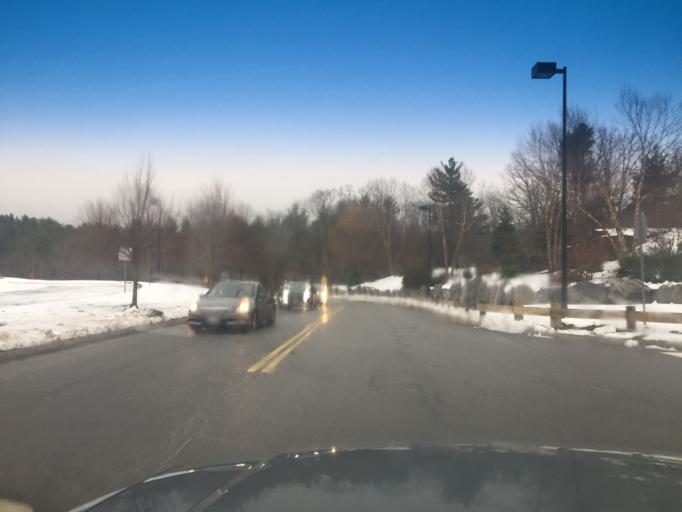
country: US
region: Massachusetts
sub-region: Middlesex County
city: Hudson
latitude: 42.3950
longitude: -71.6006
